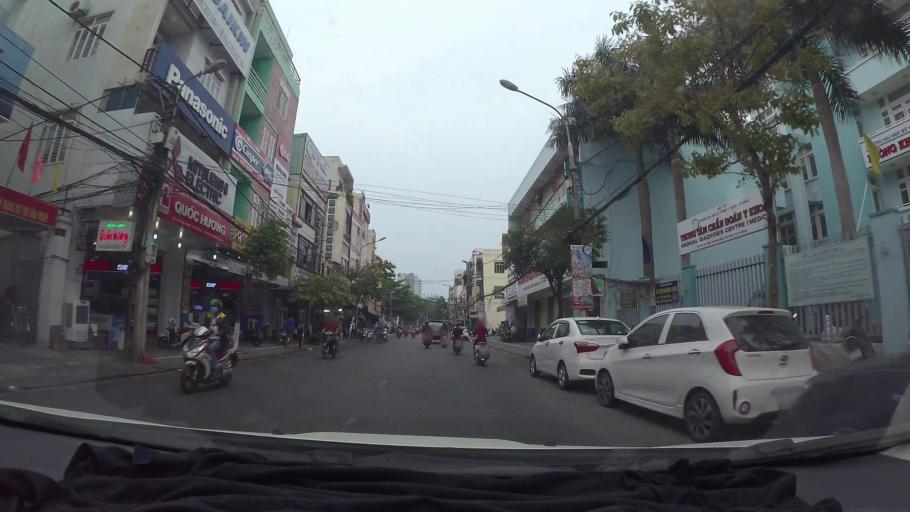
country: VN
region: Da Nang
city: Da Nang
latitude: 16.0682
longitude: 108.2185
